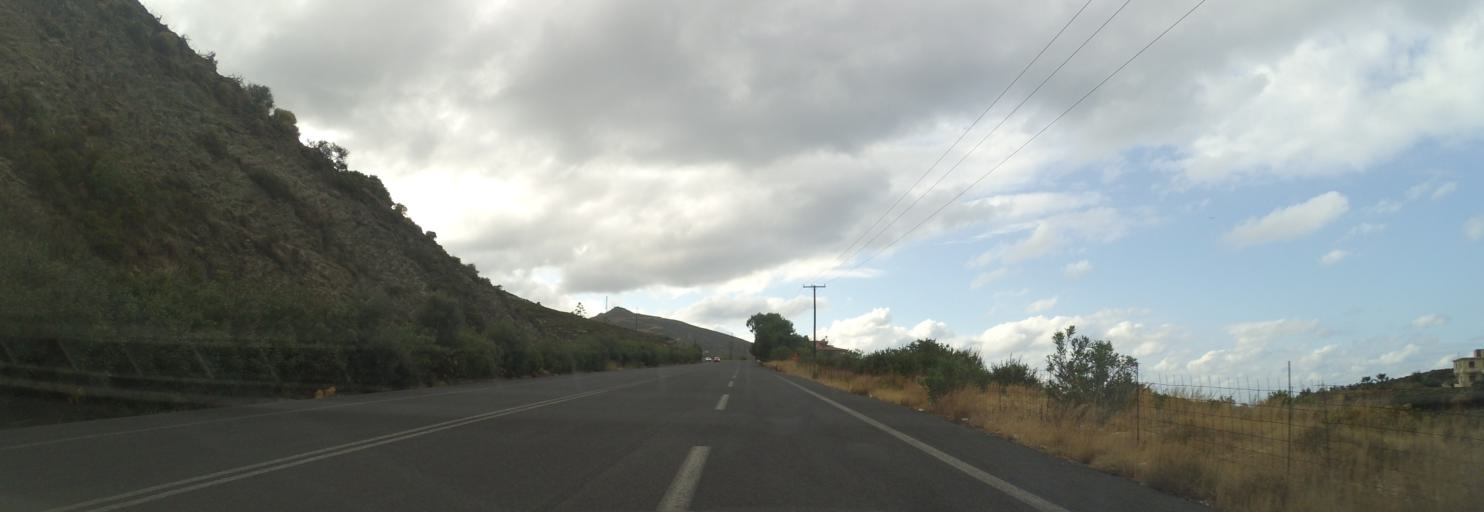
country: GR
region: Crete
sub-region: Nomos Rethymnis
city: Perama
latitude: 35.4092
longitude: 24.7728
